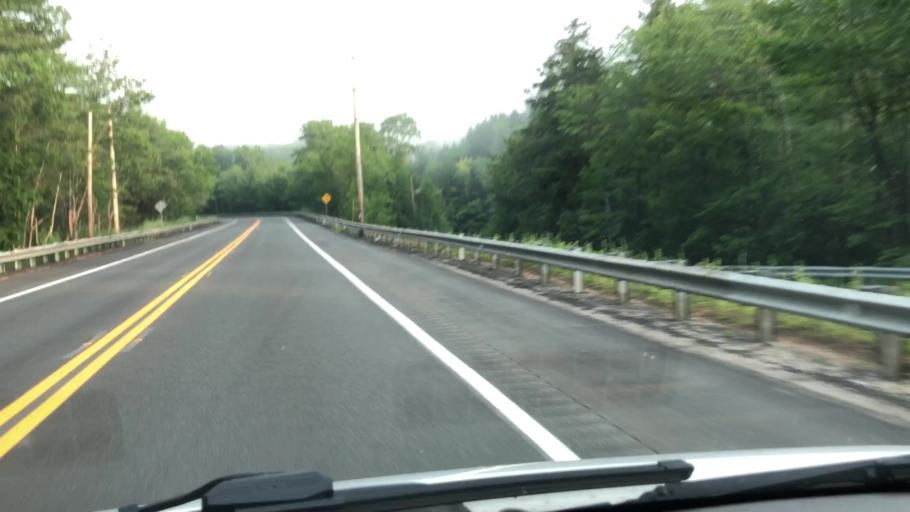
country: US
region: Massachusetts
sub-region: Hampshire County
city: Chesterfield
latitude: 42.4550
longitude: -72.8486
